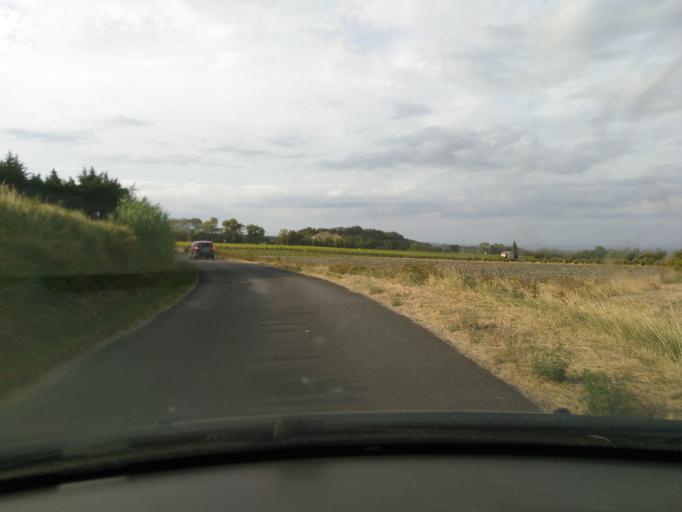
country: FR
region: Provence-Alpes-Cote d'Azur
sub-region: Departement du Vaucluse
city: Valreas
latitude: 44.4253
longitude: 5.0489
